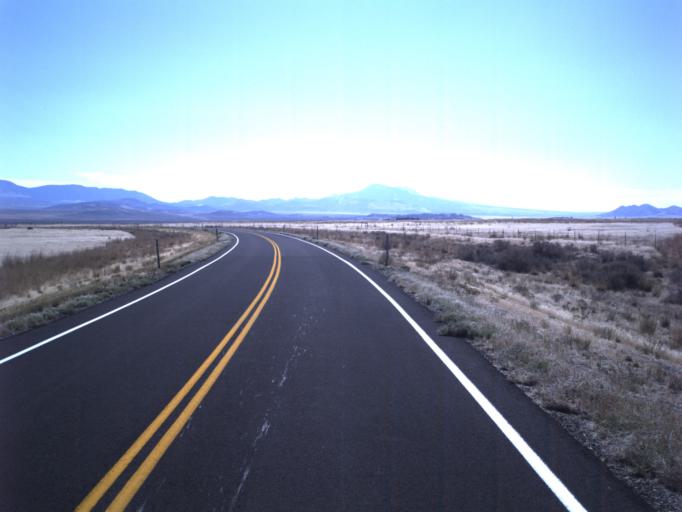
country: US
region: Utah
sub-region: Tooele County
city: Grantsville
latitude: 40.2548
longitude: -112.7390
